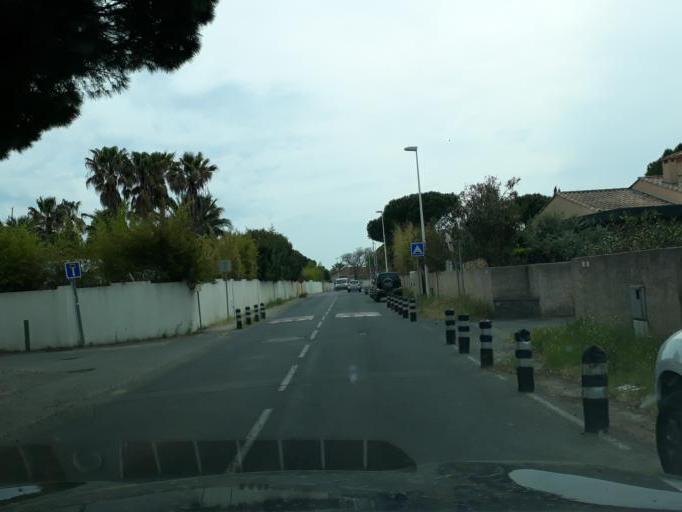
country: FR
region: Languedoc-Roussillon
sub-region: Departement de l'Herault
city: Agde
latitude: 43.2879
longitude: 3.4704
